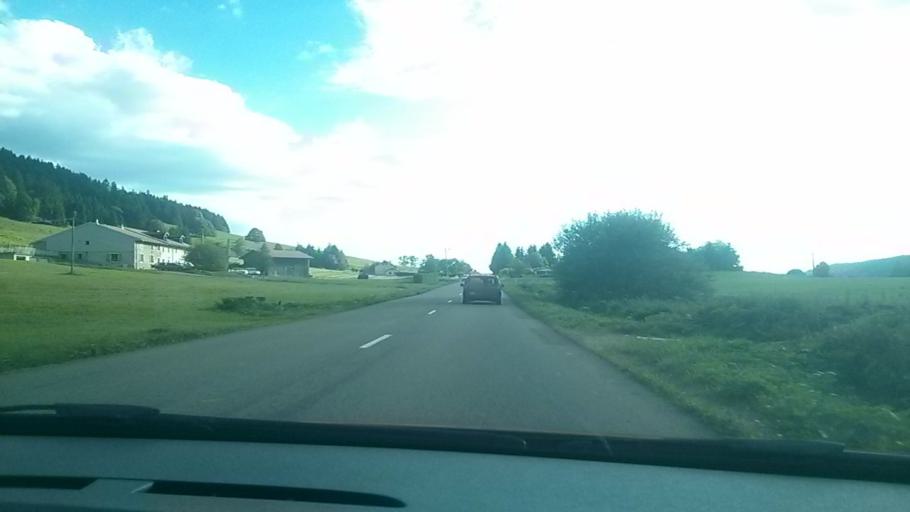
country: FR
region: Franche-Comte
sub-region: Departement du Jura
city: Les Rousses
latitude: 46.5162
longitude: 6.1174
